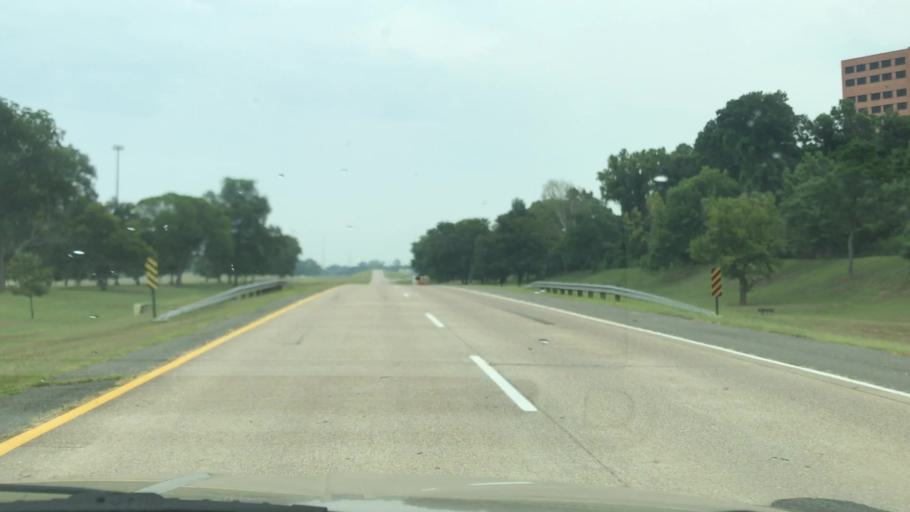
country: US
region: Louisiana
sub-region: Bossier Parish
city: Bossier City
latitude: 32.5053
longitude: -93.7216
